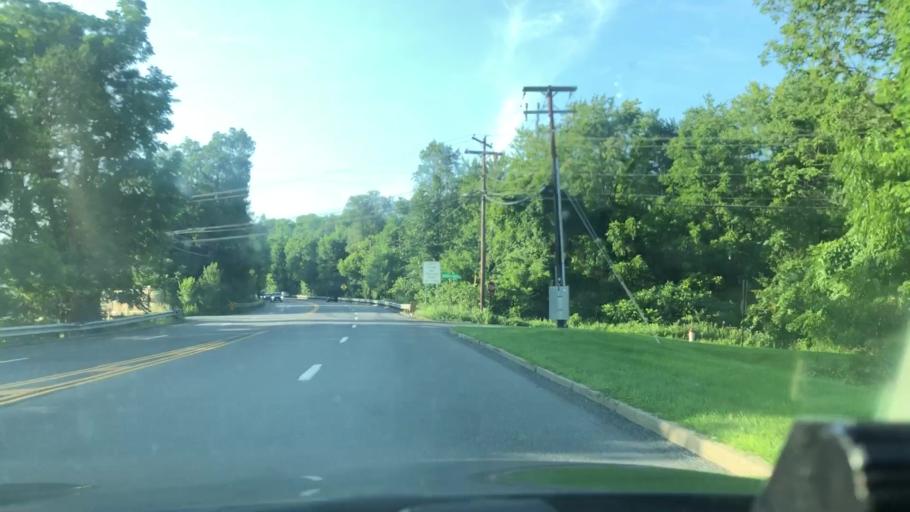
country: US
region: Pennsylvania
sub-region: Lehigh County
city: Fountain Hill
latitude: 40.5882
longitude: -75.3863
